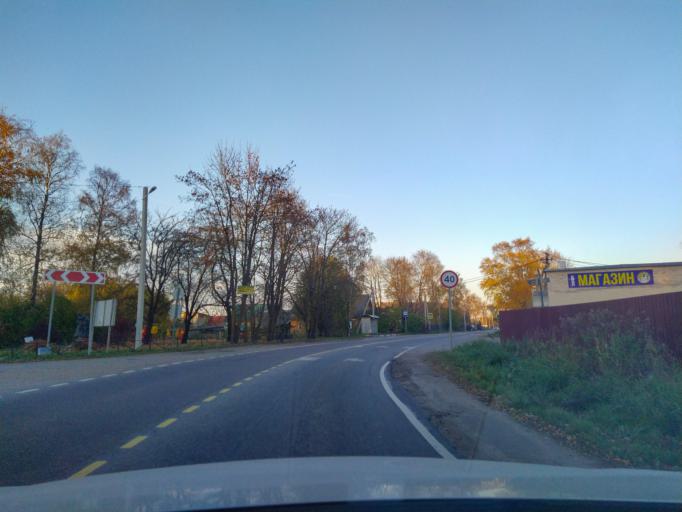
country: RU
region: Leningrad
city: Kobrinskoye
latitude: 59.4733
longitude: 30.1216
